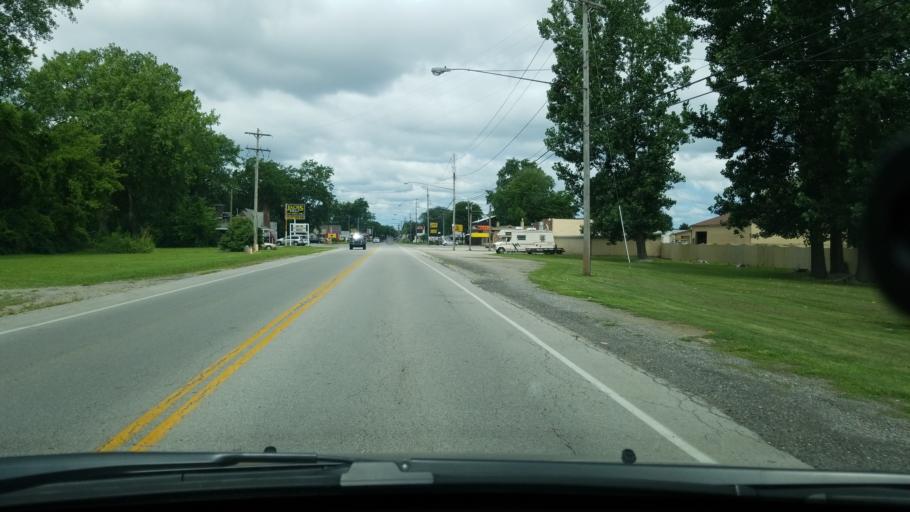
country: US
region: Ohio
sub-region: Erie County
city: Sandusky
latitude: 41.4352
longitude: -82.6653
